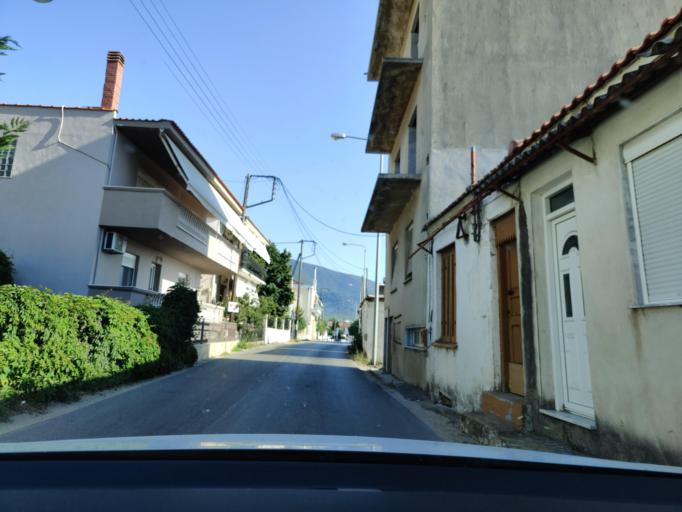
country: GR
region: East Macedonia and Thrace
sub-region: Nomos Kavalas
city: Prinos
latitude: 40.7102
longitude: 24.5340
